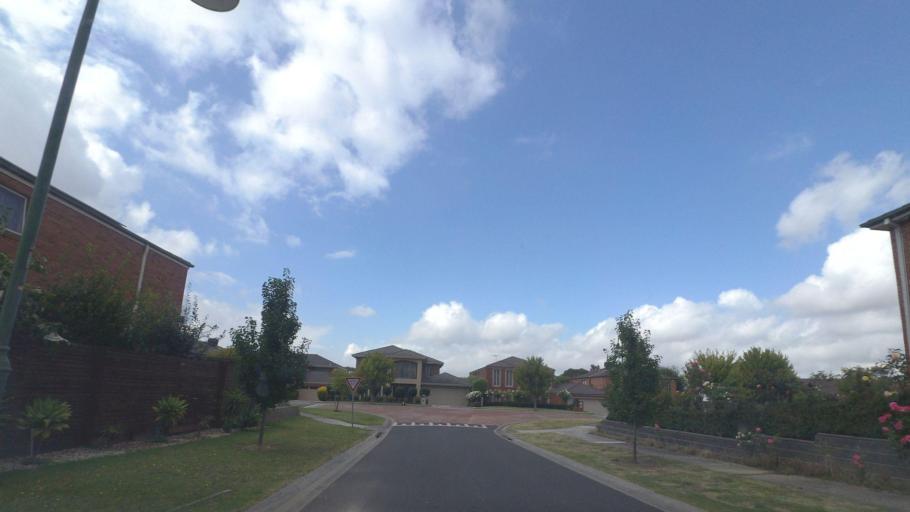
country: AU
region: Victoria
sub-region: Knox
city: Scoresby
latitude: -37.8923
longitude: 145.2266
